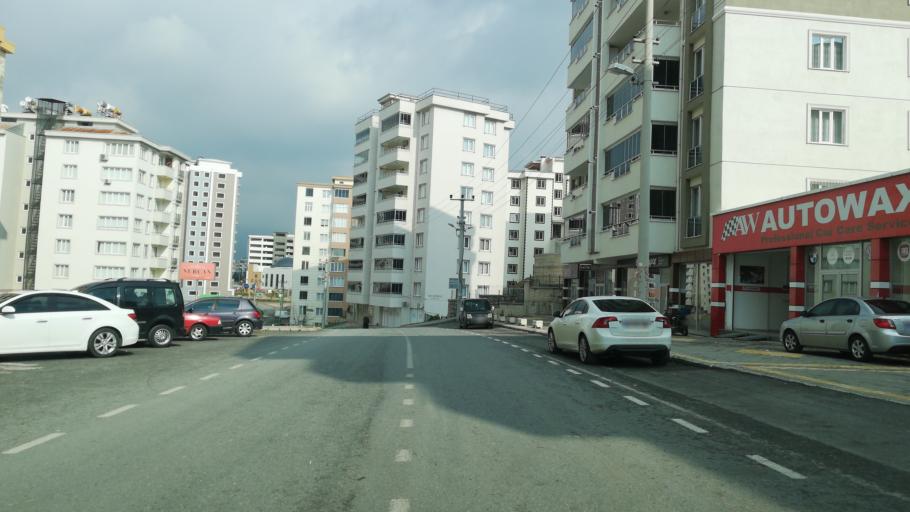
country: TR
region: Kahramanmaras
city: Kahramanmaras
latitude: 37.5799
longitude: 36.8957
